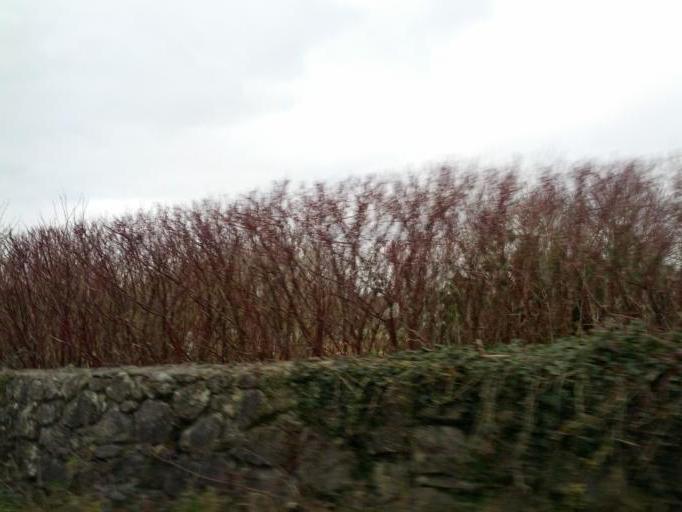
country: IE
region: Connaught
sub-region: County Galway
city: Oranmore
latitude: 53.2195
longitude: -8.8927
